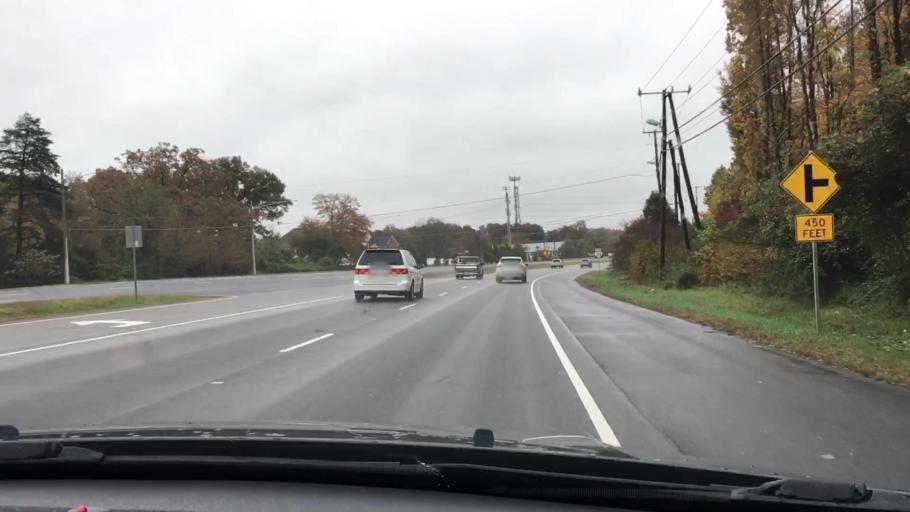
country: US
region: Virginia
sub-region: Prince William County
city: Lake Ridge
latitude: 38.7181
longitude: -77.2689
